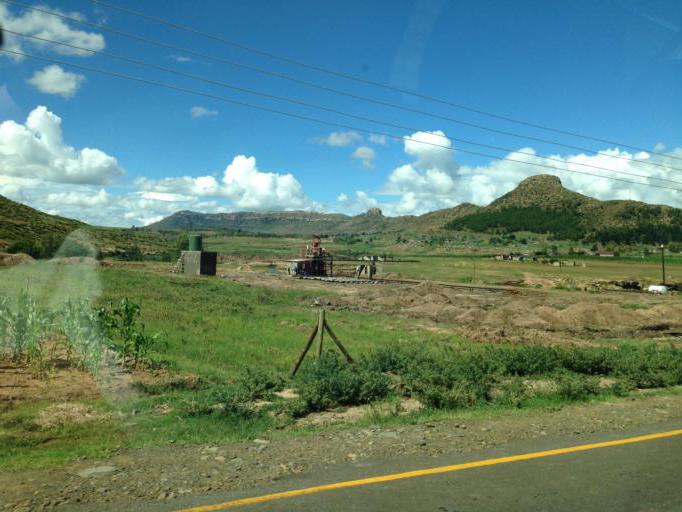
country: LS
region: Mafeteng
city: Mafeteng
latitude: -29.6940
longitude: 27.4426
